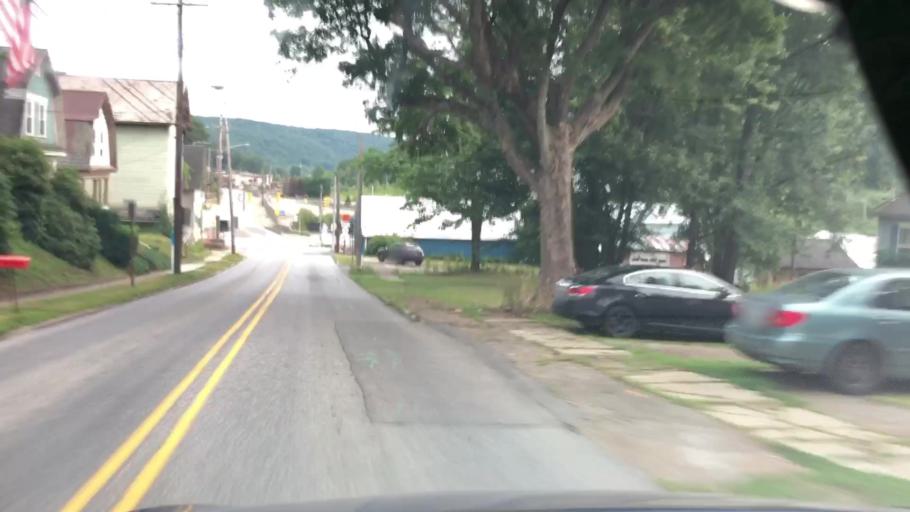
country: US
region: Pennsylvania
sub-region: Venango County
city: Hasson Heights
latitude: 41.4700
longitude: -79.6919
